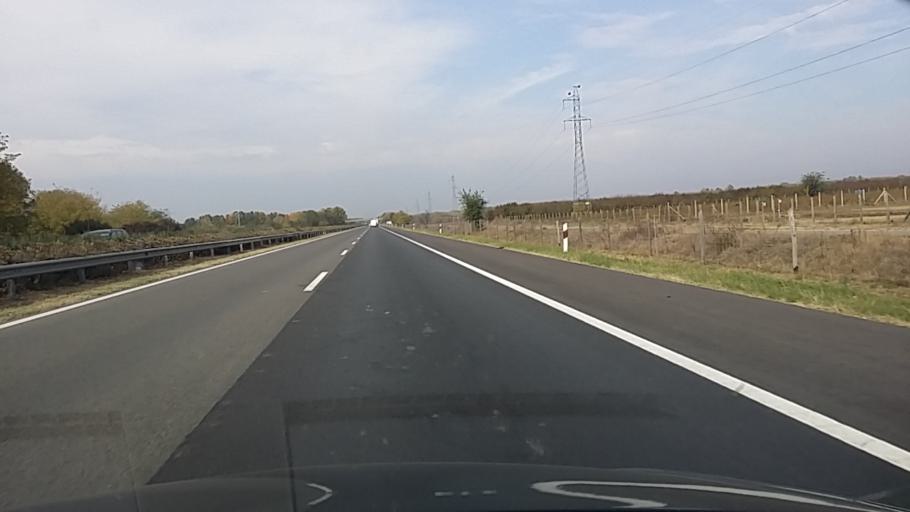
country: HU
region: Pest
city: Taborfalva
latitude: 47.0880
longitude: 19.5234
